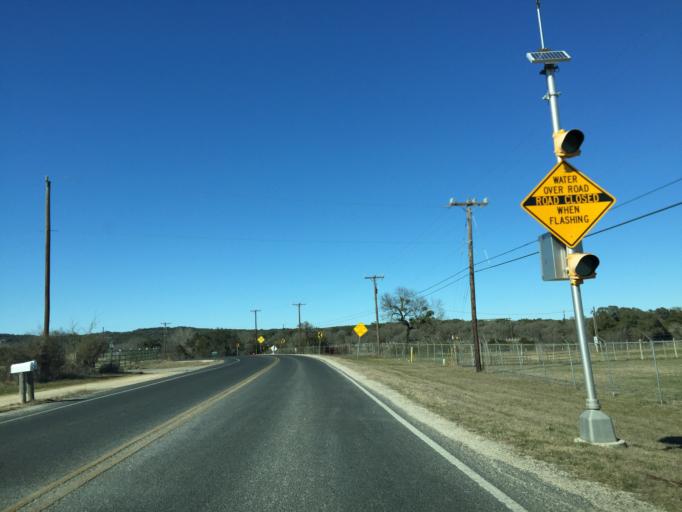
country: US
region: Texas
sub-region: Comal County
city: Bulverde
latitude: 29.7468
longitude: -98.4068
